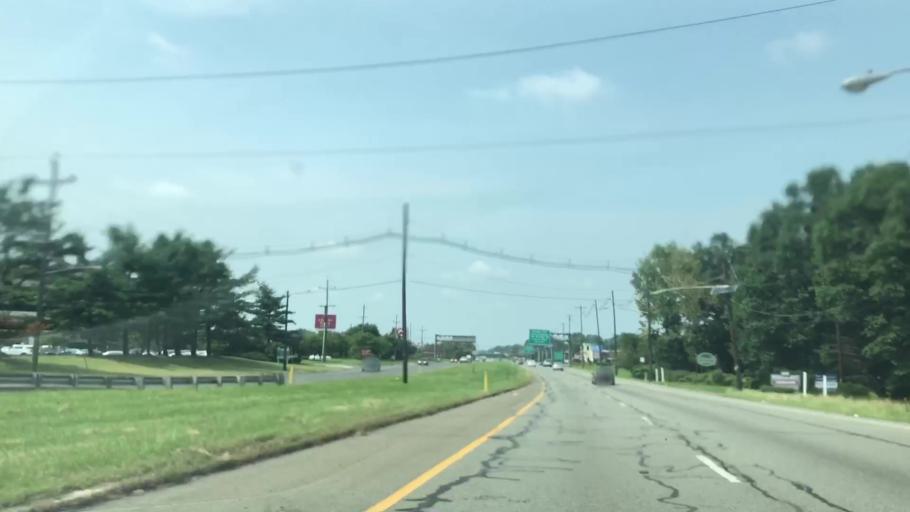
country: US
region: New Jersey
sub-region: Passaic County
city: Singac
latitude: 40.8924
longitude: -74.2668
